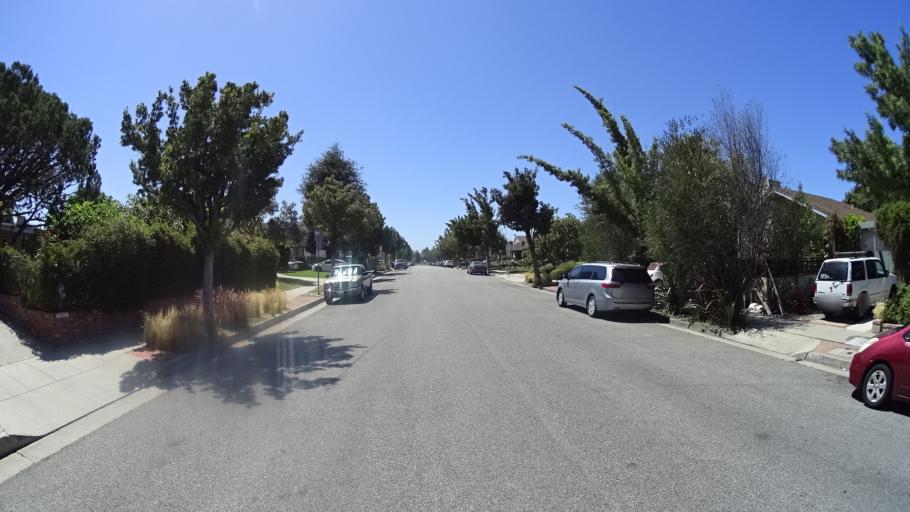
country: US
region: California
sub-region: Los Angeles County
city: Westwood, Los Angeles
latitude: 34.0245
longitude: -118.4521
